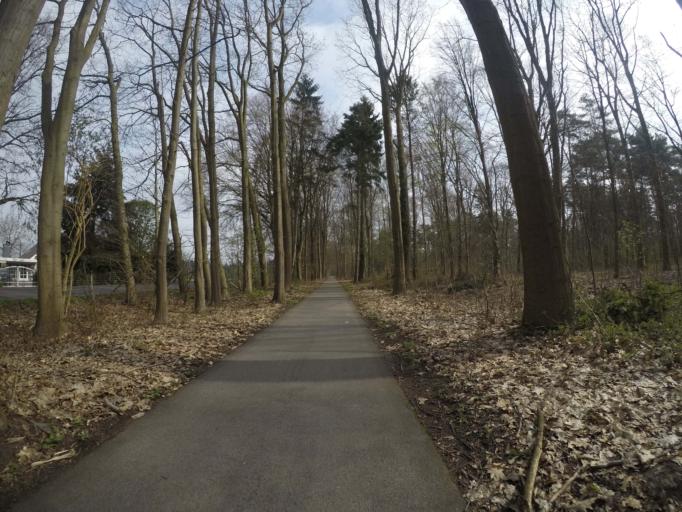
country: DE
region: North Rhine-Westphalia
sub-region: Regierungsbezirk Munster
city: Isselburg
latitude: 51.8364
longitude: 6.4953
